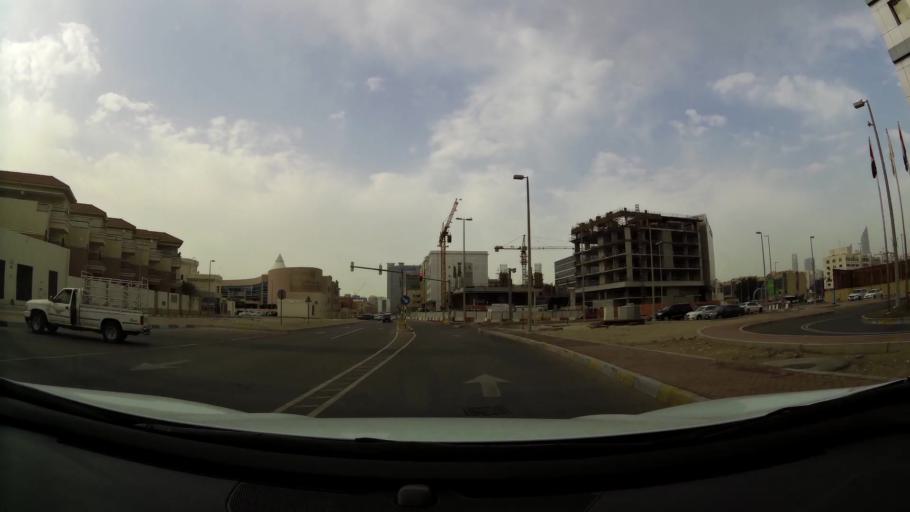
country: AE
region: Abu Dhabi
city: Abu Dhabi
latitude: 24.4773
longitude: 54.3833
